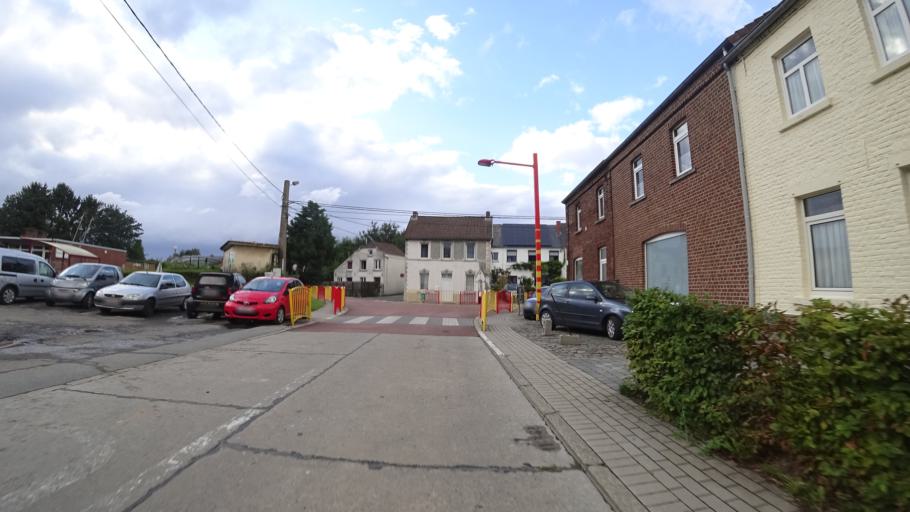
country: BE
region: Wallonia
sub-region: Province du Brabant Wallon
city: Chastre-Villeroux-Blanmont
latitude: 50.6369
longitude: 4.6640
